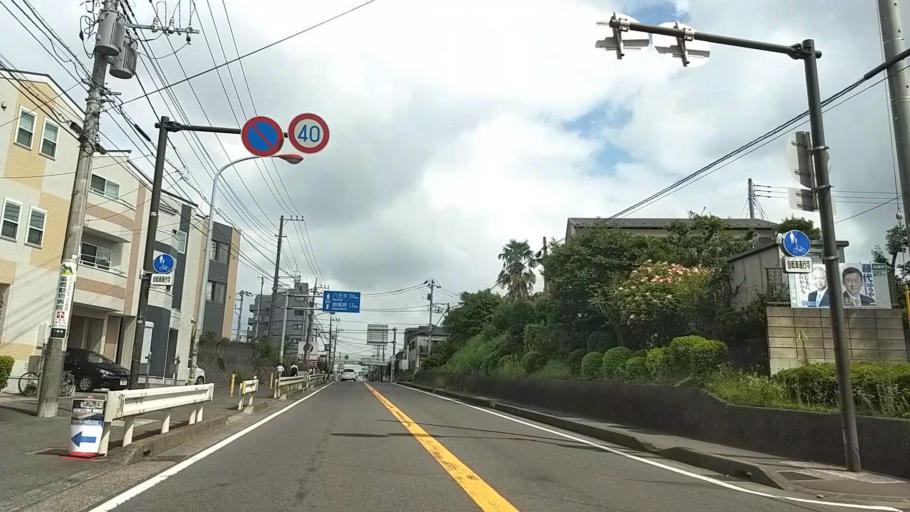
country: JP
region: Kanagawa
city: Minami-rinkan
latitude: 35.5026
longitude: 139.4658
